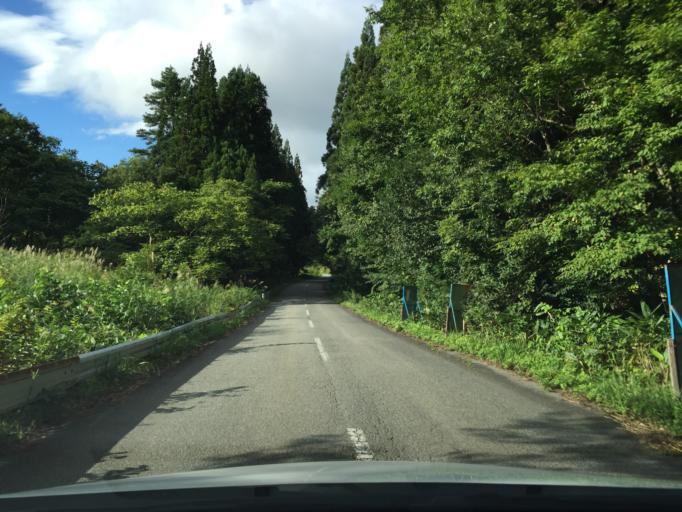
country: JP
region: Yamagata
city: Yonezawa
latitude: 37.9087
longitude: 140.2051
